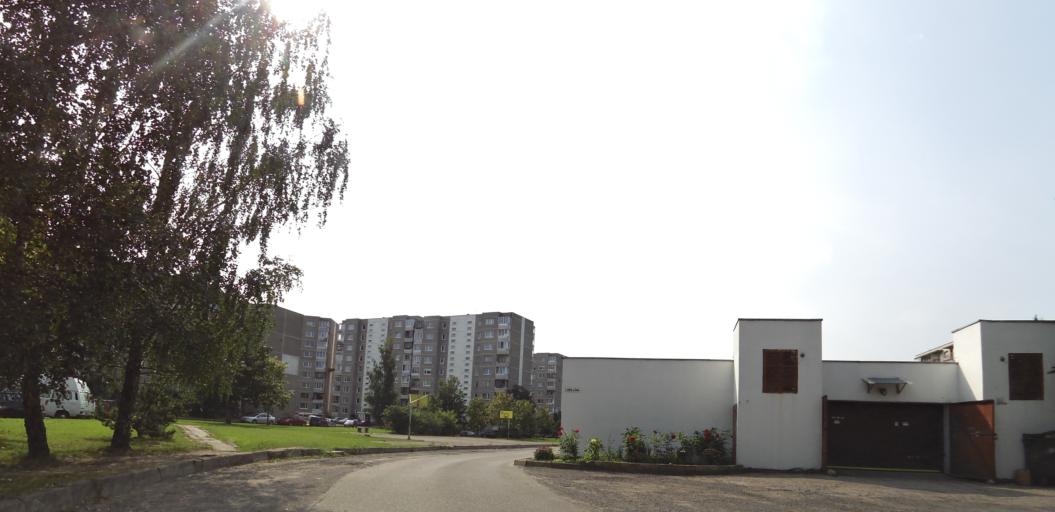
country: LT
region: Vilnius County
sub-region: Vilnius
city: Fabijoniskes
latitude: 54.7409
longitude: 25.2371
